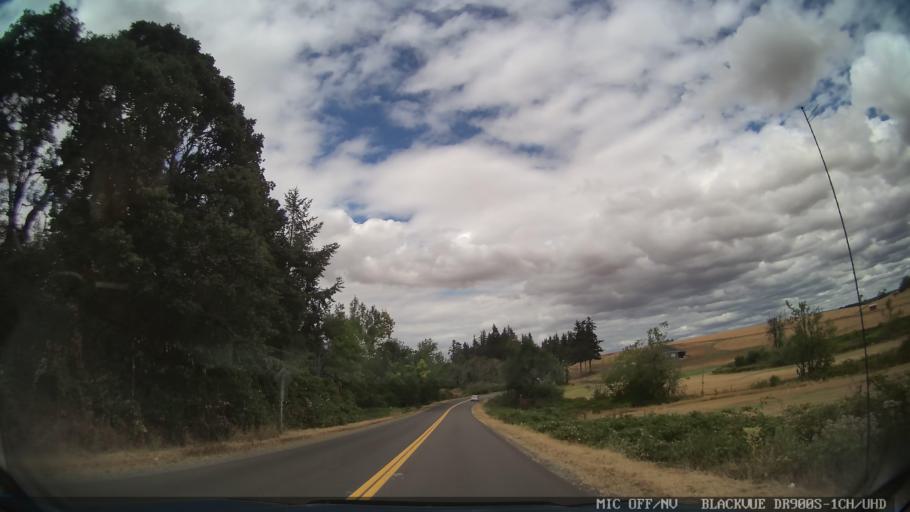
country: US
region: Oregon
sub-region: Marion County
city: Aumsville
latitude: 44.8616
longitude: -122.8511
